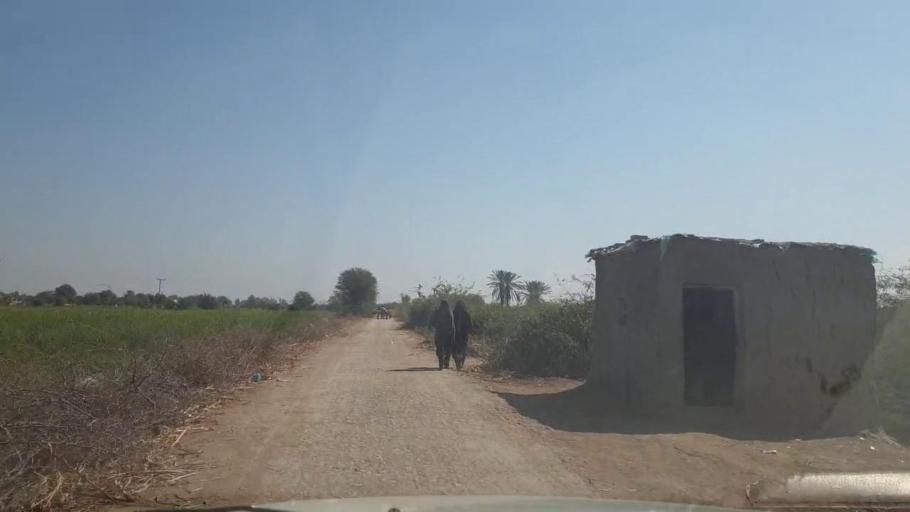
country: PK
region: Sindh
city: Mirpur Khas
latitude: 25.5440
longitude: 69.1926
